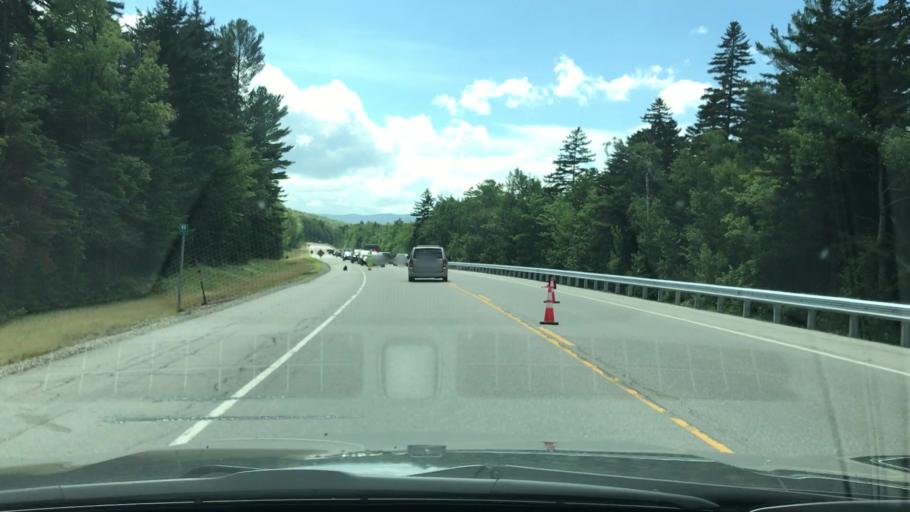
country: US
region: New Hampshire
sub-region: Coos County
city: Gorham
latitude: 44.3704
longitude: -71.3002
